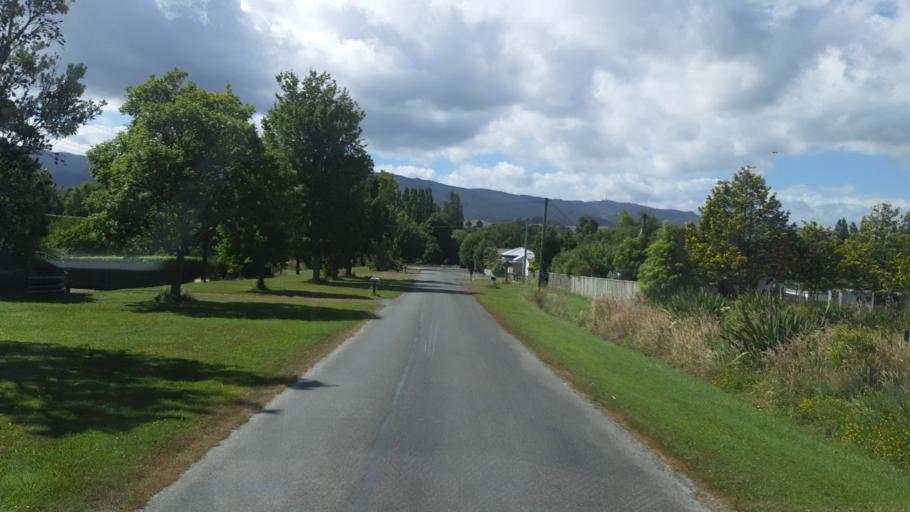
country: NZ
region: Manawatu-Wanganui
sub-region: Palmerston North City
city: Palmerston North
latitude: -40.1718
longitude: 175.7926
